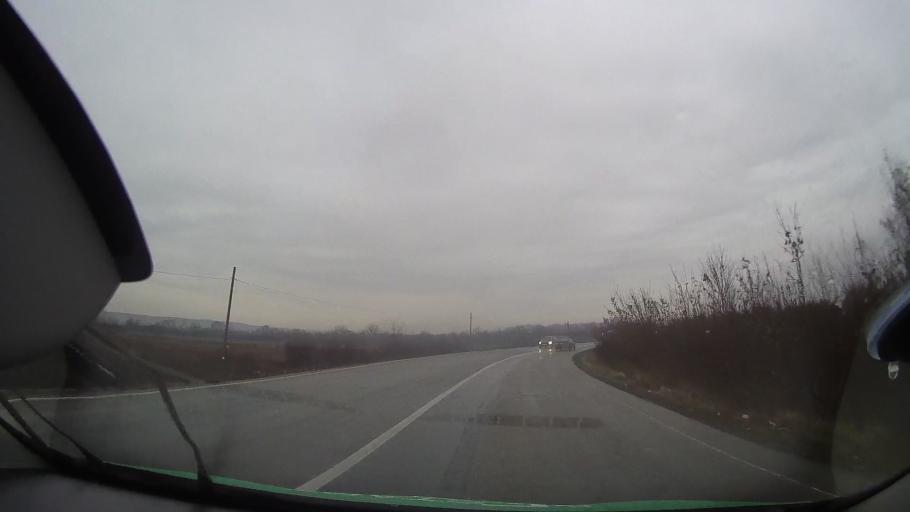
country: RO
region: Bihor
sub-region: Comuna Sambata
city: Sambata
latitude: 46.7934
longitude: 22.2035
